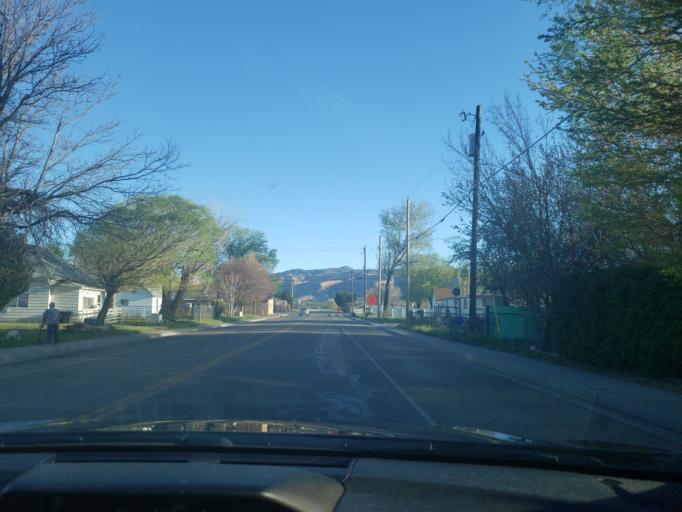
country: US
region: Colorado
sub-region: Mesa County
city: Fruita
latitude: 39.1602
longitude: -108.7384
